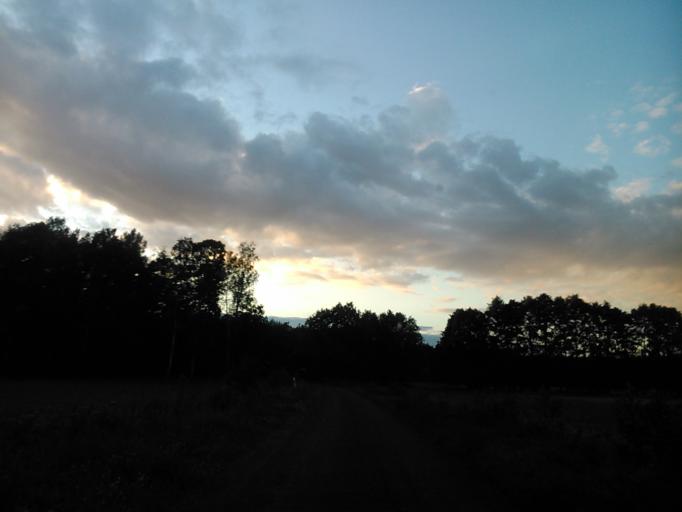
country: PL
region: Kujawsko-Pomorskie
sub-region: Powiat golubsko-dobrzynski
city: Radomin
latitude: 53.1619
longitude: 19.1441
